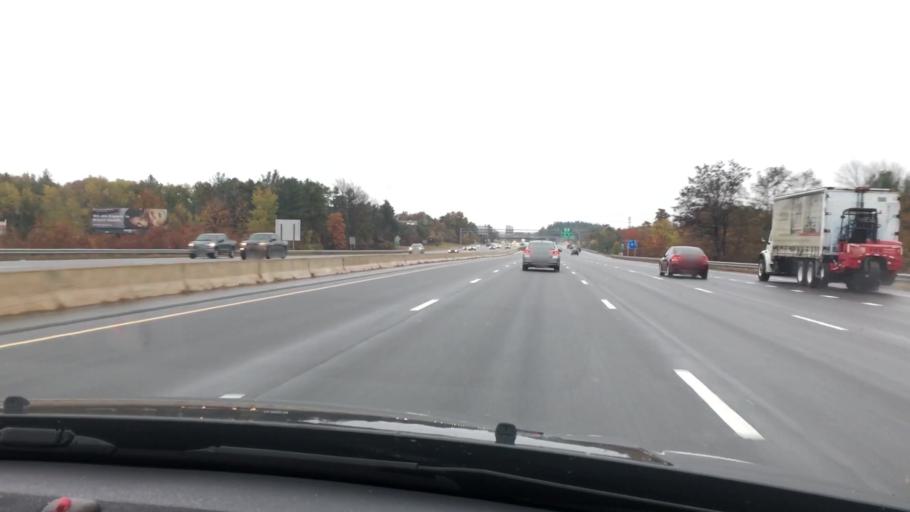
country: US
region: New Hampshire
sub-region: Hillsborough County
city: Nashua
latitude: 42.7582
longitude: -71.4934
